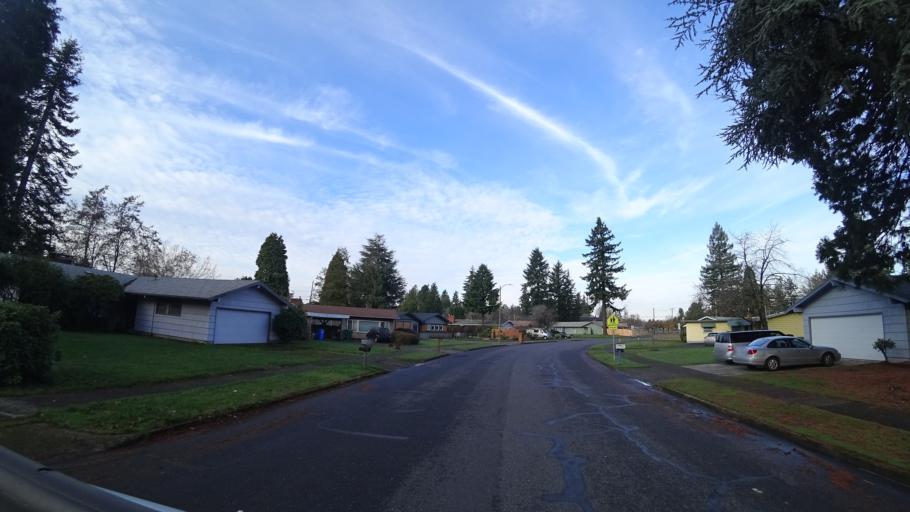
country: US
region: Oregon
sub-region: Multnomah County
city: Lents
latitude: 45.5310
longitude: -122.5279
